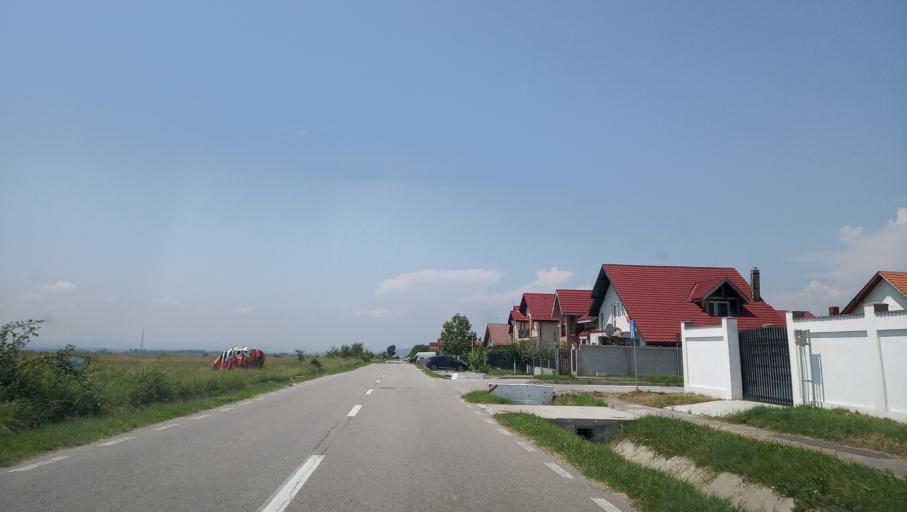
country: RO
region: Gorj
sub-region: Comuna Turcinesti
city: Turcinesti
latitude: 45.0656
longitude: 23.3350
